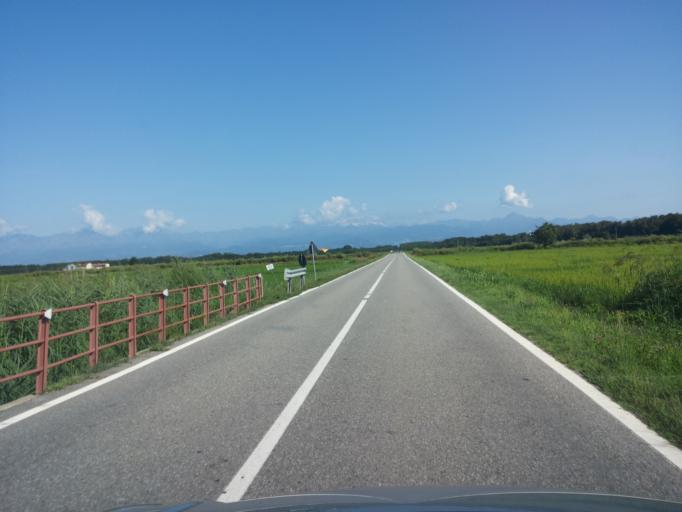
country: IT
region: Piedmont
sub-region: Provincia di Vercelli
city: Balocco
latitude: 45.4608
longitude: 8.2777
